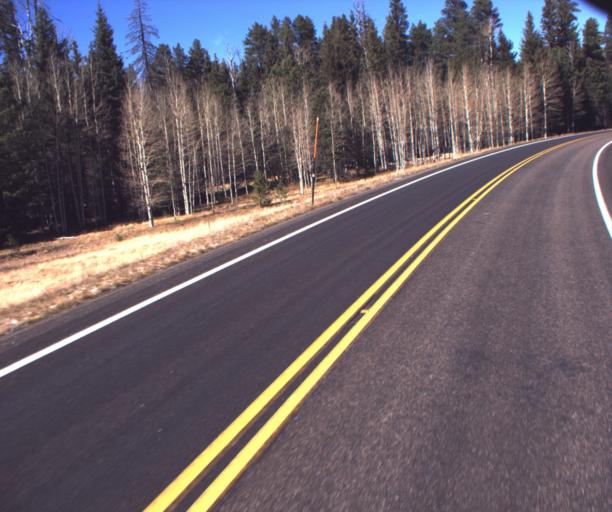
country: US
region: Arizona
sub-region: Coconino County
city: Grand Canyon
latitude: 36.5050
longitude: -112.1409
